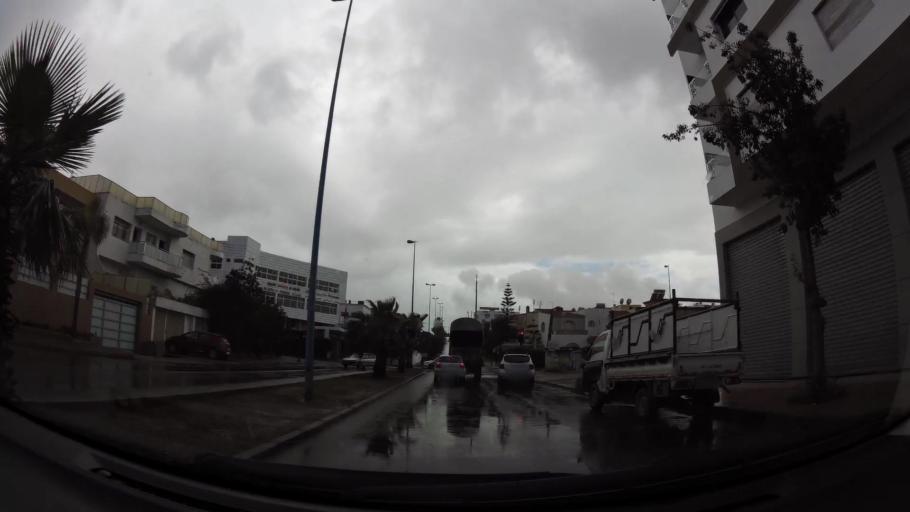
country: MA
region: Grand Casablanca
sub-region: Casablanca
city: Casablanca
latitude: 33.5438
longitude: -7.6731
